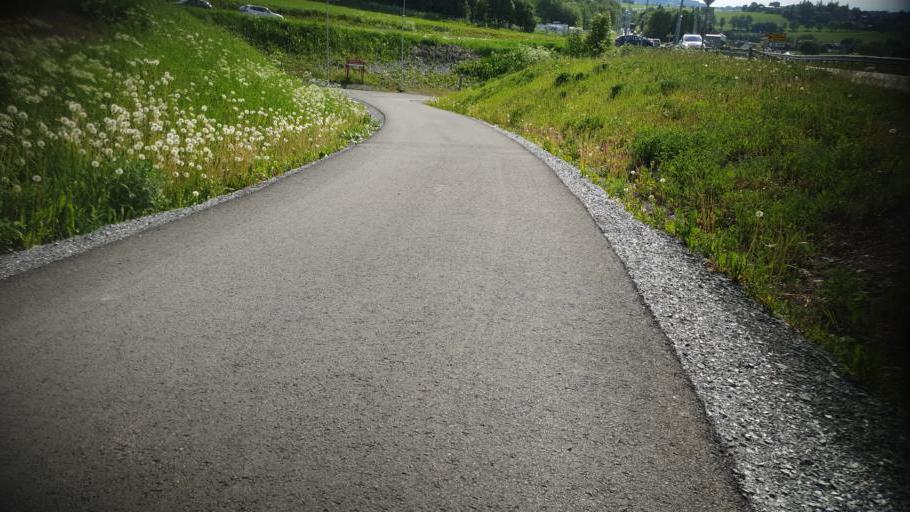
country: NO
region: Sor-Trondelag
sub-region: Malvik
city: Malvik
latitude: 63.4311
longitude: 10.5689
